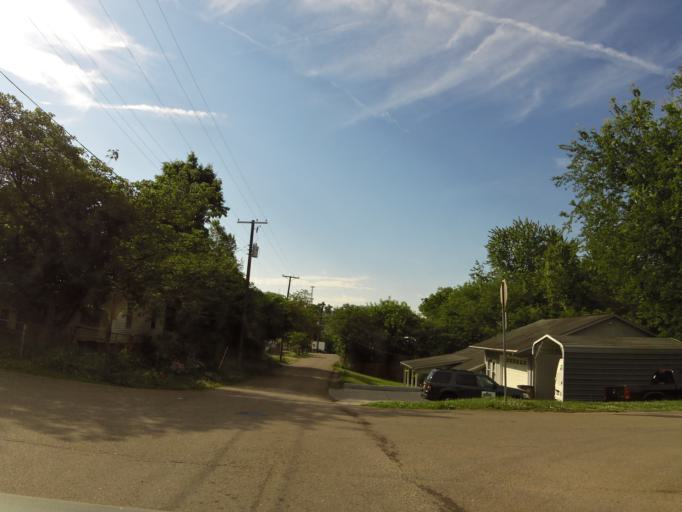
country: US
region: Tennessee
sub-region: Knox County
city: Knoxville
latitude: 35.9945
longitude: -83.9094
